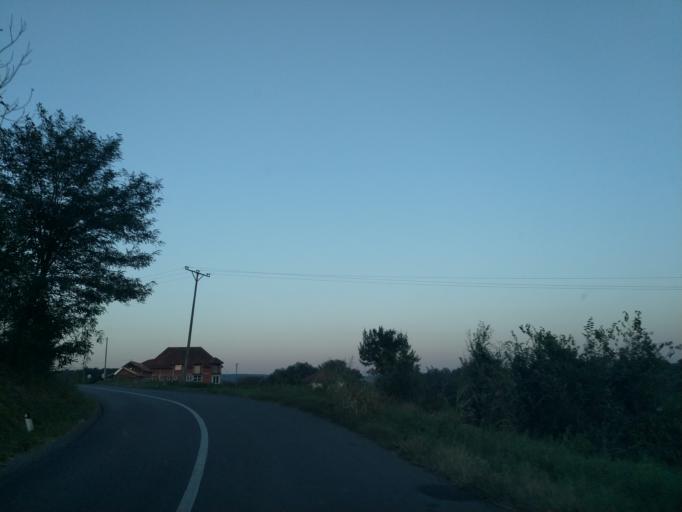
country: RS
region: Central Serbia
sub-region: Rasinski Okrug
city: Krusevac
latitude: 43.6208
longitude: 21.3100
